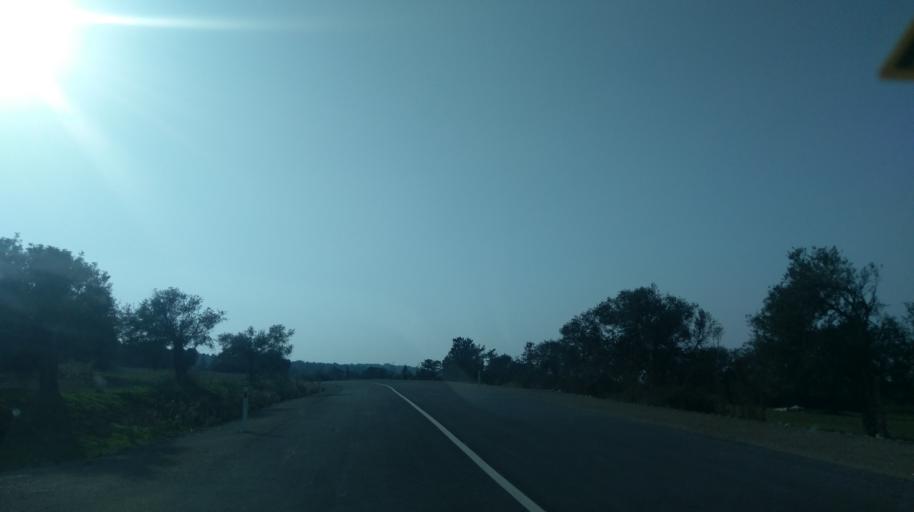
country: CY
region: Ammochostos
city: Leonarisso
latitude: 35.5366
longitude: 34.2362
